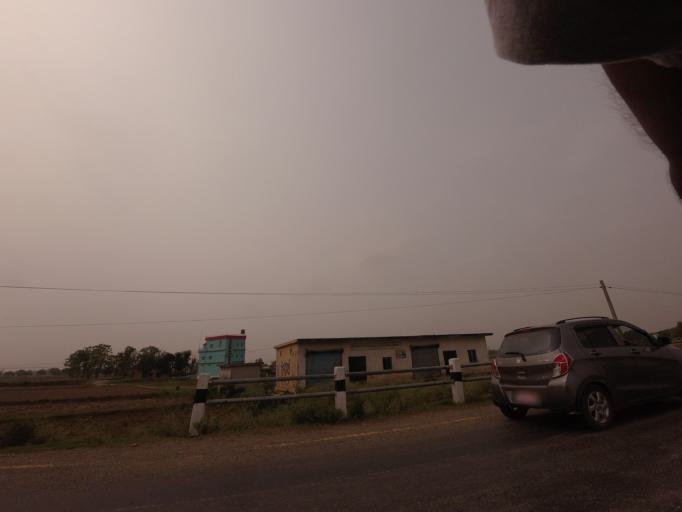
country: IN
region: Uttar Pradesh
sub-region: Maharajganj
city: Nautanwa
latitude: 27.5011
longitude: 83.3392
